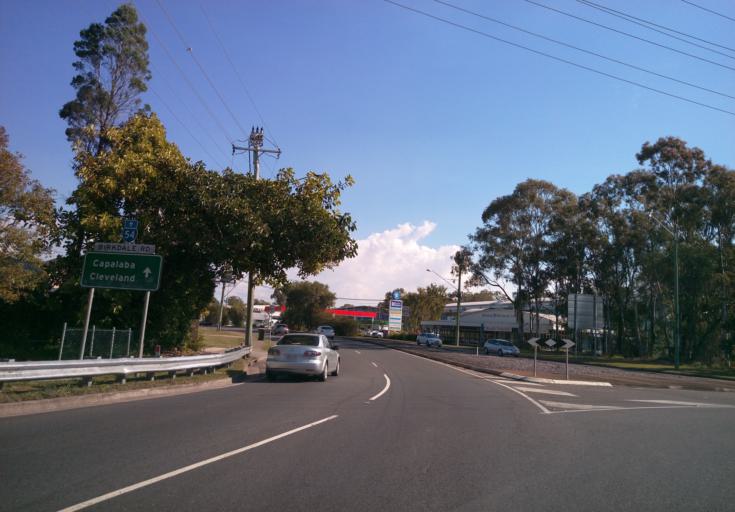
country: AU
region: Queensland
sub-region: Redland
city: Wellington Point
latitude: -27.4939
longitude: 153.2141
